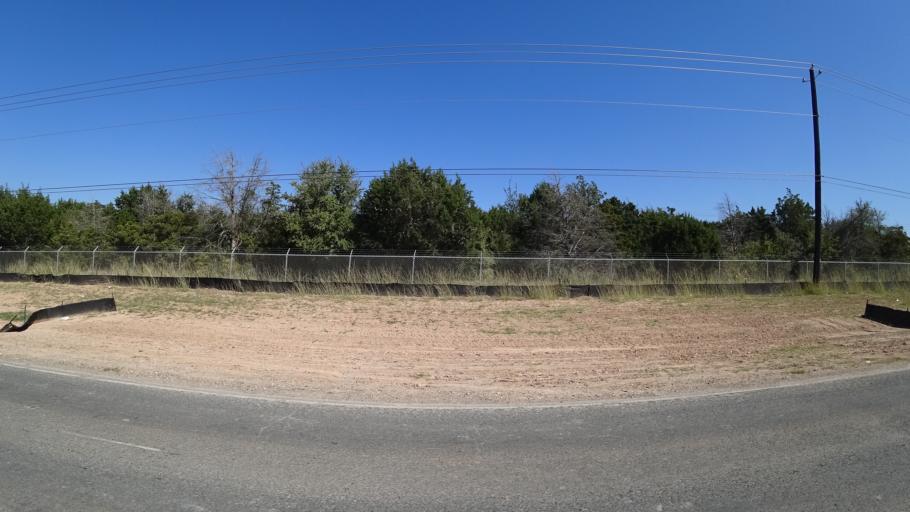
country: US
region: Texas
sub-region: Travis County
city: Hornsby Bend
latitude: 30.2791
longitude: -97.6076
